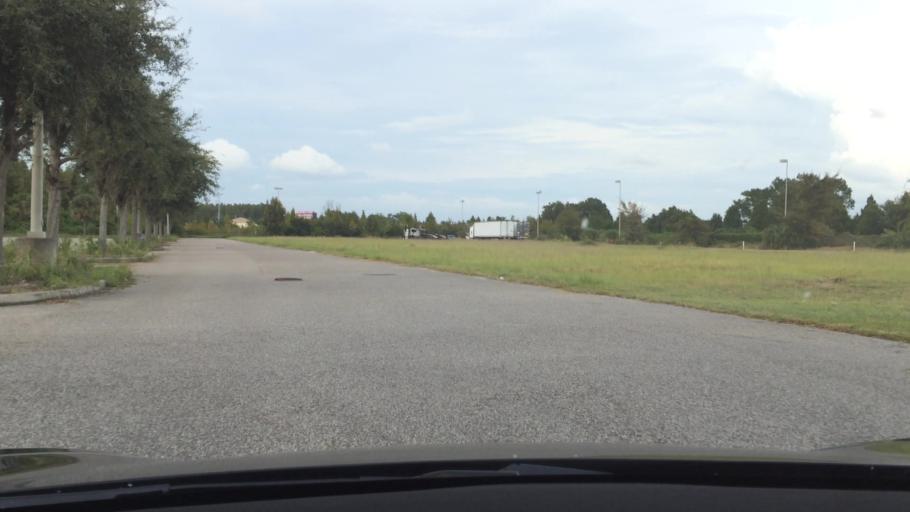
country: US
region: Florida
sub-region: Hillsborough County
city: Lutz
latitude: 28.1741
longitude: -82.4703
